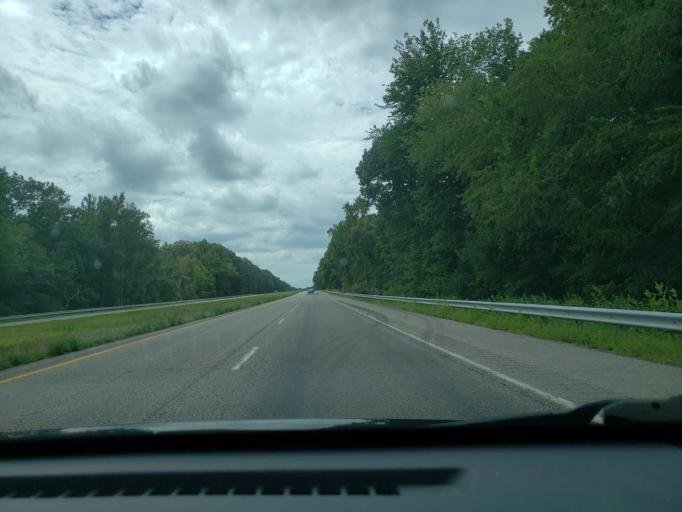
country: US
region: Delaware
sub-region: New Castle County
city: Townsend
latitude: 39.3396
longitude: -75.8338
